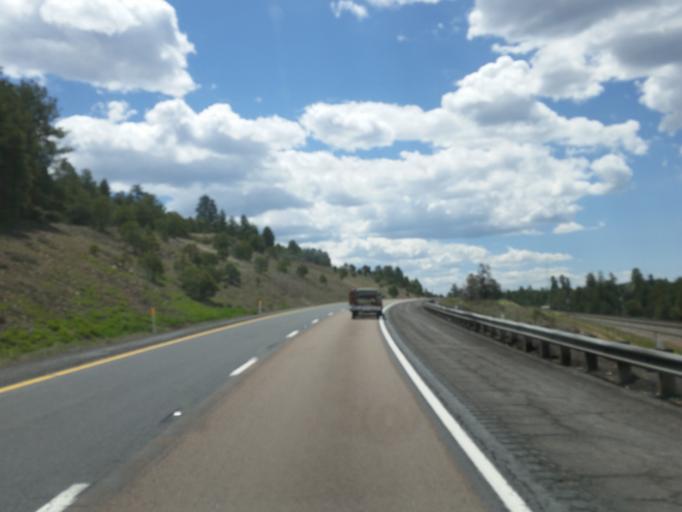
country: US
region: Arizona
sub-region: Coconino County
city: Flagstaff
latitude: 35.2106
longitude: -111.7734
